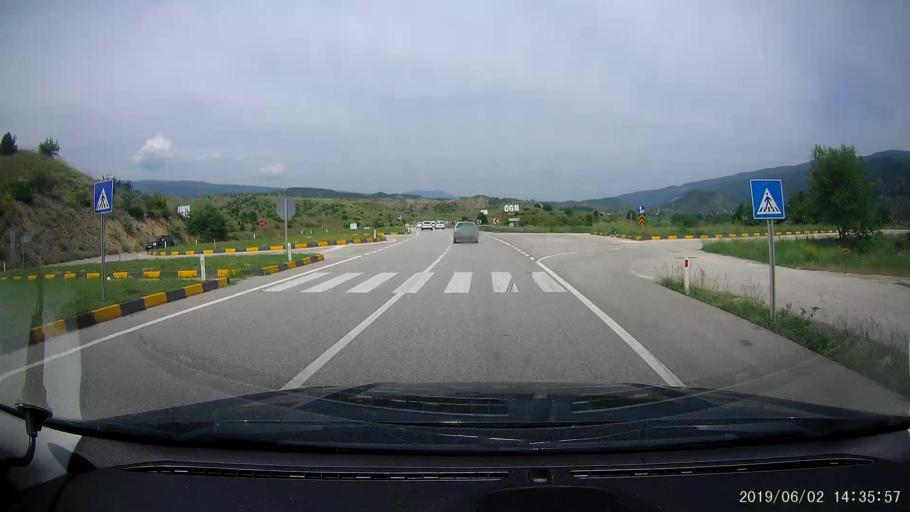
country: TR
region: Kastamonu
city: Tosya
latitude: 41.0432
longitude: 34.2260
